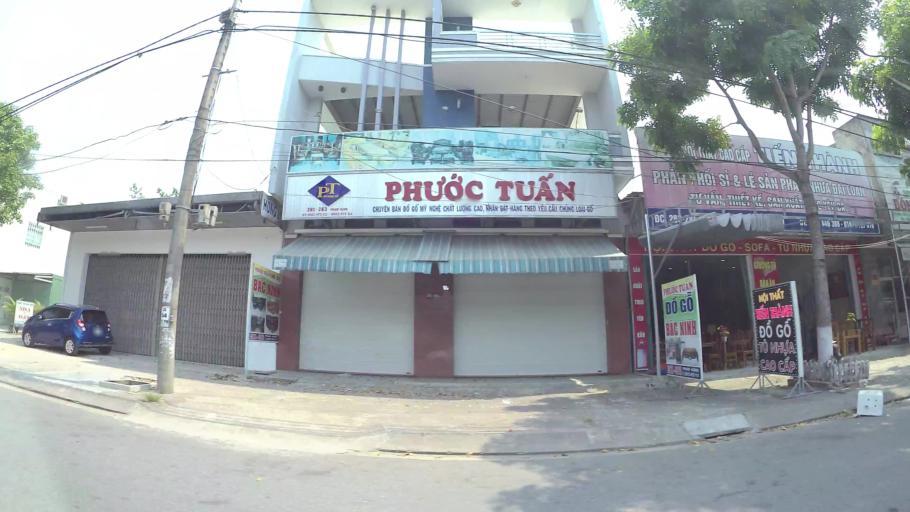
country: VN
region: Da Nang
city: Cam Le
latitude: 15.9884
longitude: 108.2078
